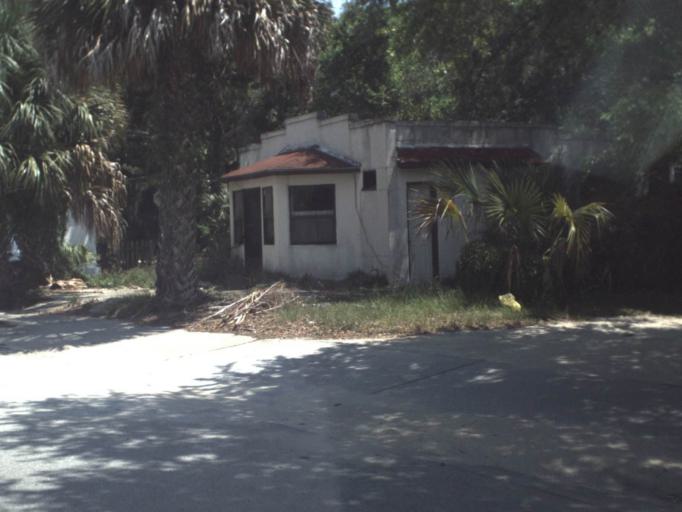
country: US
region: Florida
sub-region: Saint Johns County
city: Saint Augustine
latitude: 29.8881
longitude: -81.2915
